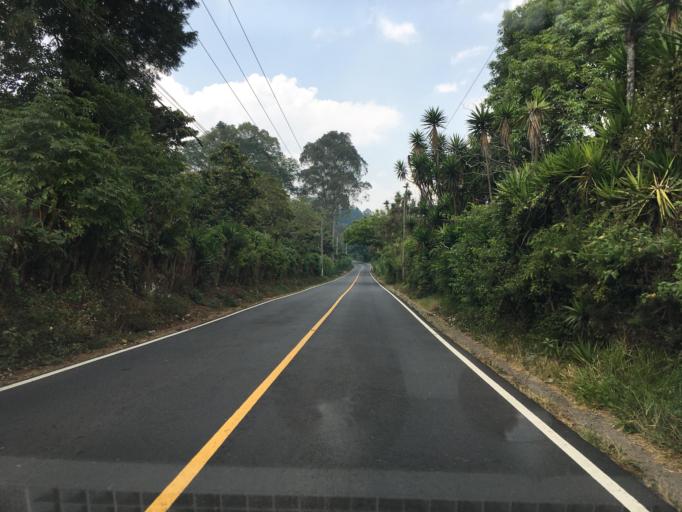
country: GT
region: Guatemala
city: Villa Canales
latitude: 14.4179
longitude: -90.5292
